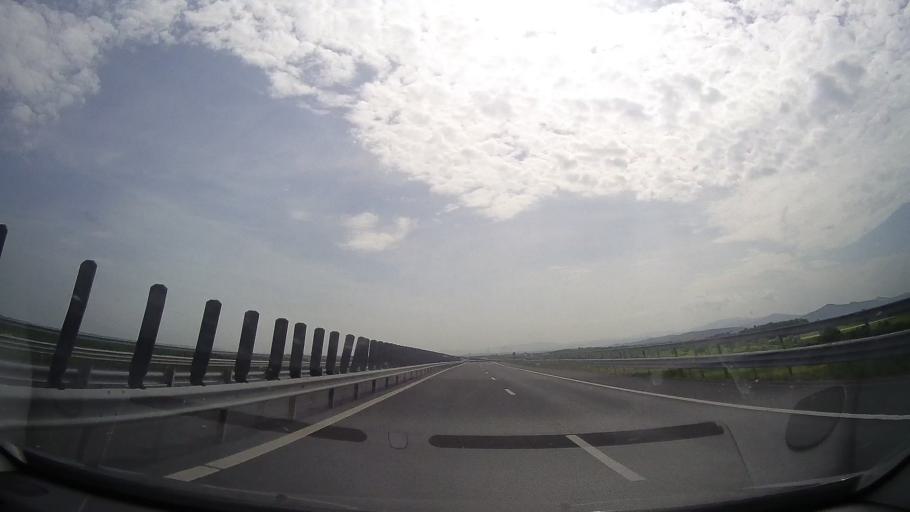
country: RO
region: Timis
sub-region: Comuna Manastiur
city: Manastiur
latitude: 45.8172
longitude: 22.0325
